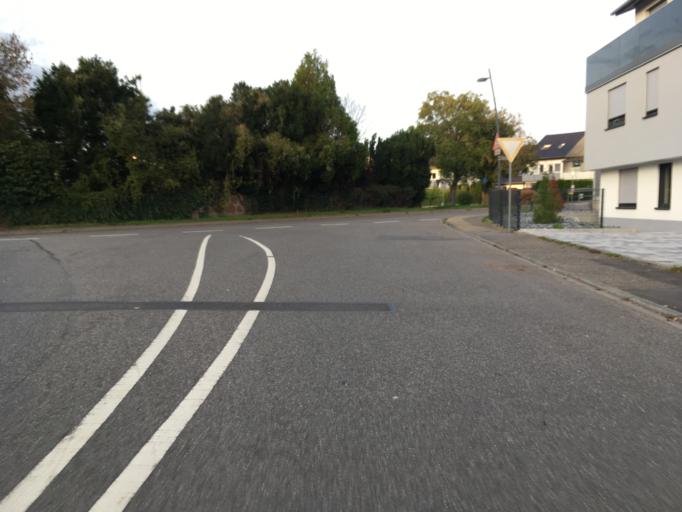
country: DE
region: Baden-Wuerttemberg
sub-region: Karlsruhe Region
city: Nussloch
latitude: 49.3262
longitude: 8.6839
